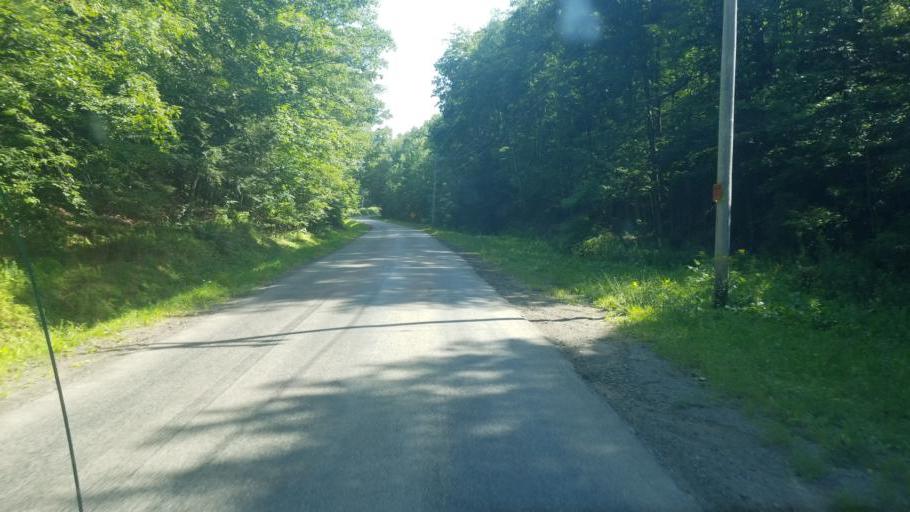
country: US
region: New York
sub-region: Allegany County
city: Bolivar
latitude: 42.0761
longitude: -78.0610
